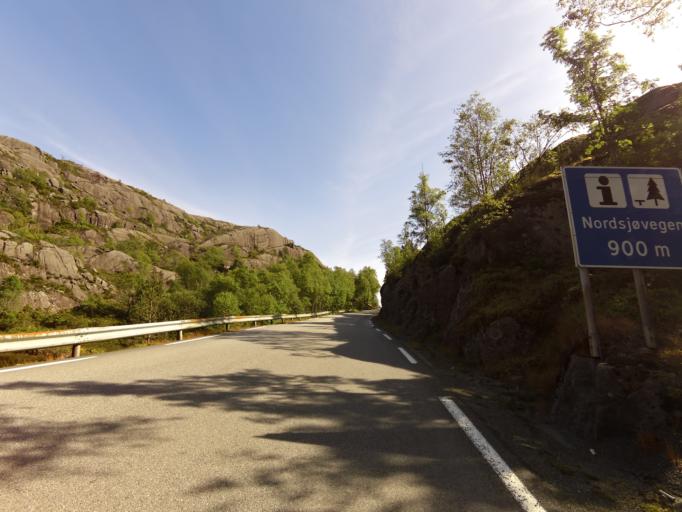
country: NO
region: Rogaland
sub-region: Sokndal
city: Hauge i Dalane
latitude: 58.3369
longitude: 6.3488
